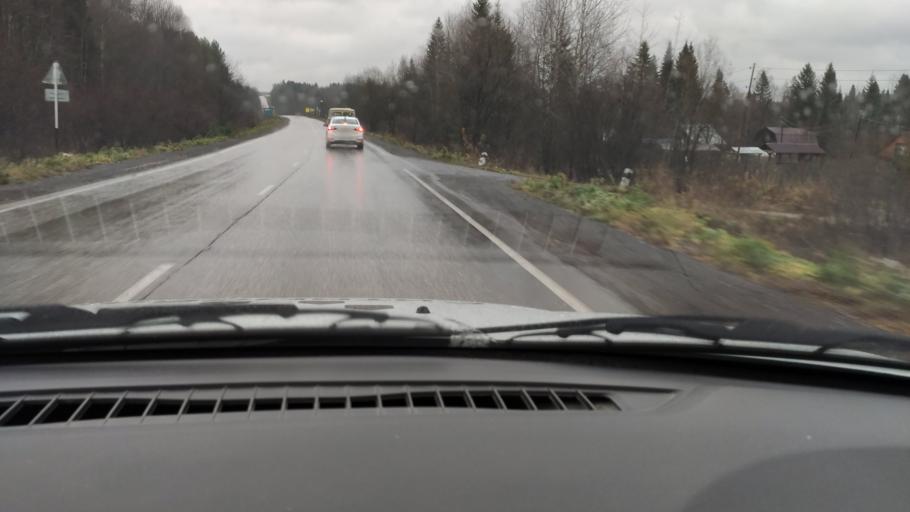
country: RU
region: Perm
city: Novyye Lyady
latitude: 58.0250
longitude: 56.6716
